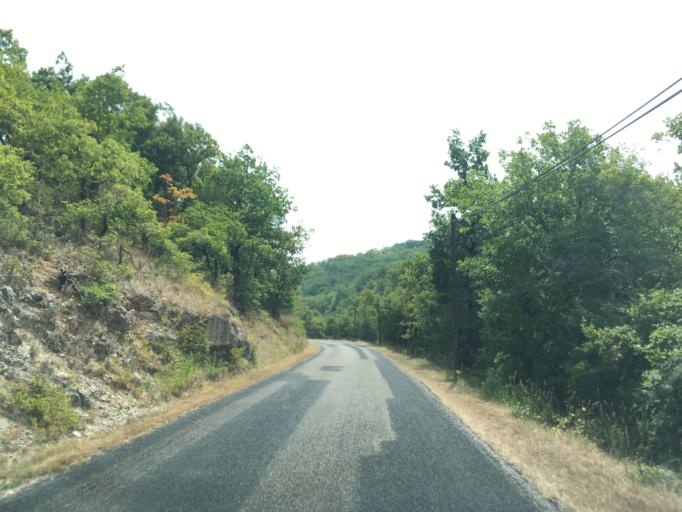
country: FR
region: Midi-Pyrenees
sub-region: Departement du Lot
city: Le Vigan
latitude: 44.7430
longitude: 1.5120
